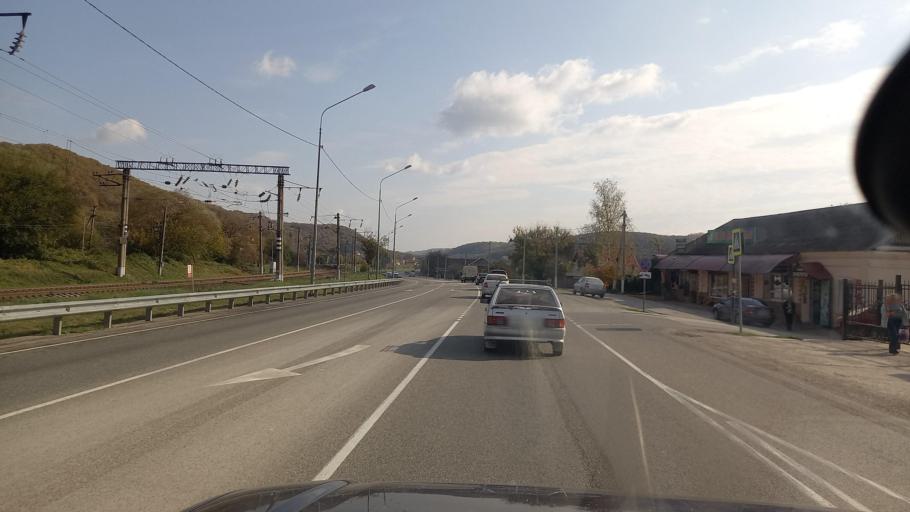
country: RU
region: Krasnodarskiy
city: Krymsk
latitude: 44.8683
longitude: 37.8720
